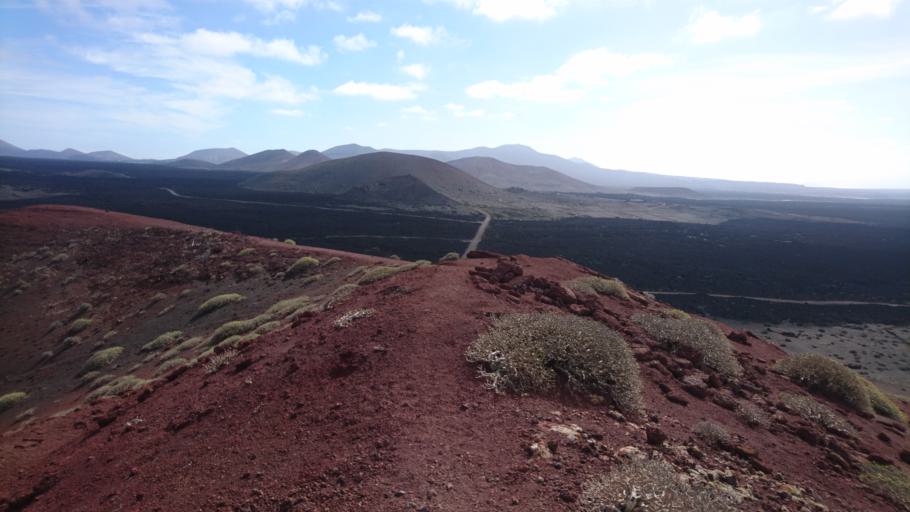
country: ES
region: Canary Islands
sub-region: Provincia de Las Palmas
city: Yaiza
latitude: 28.9883
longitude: -13.8159
